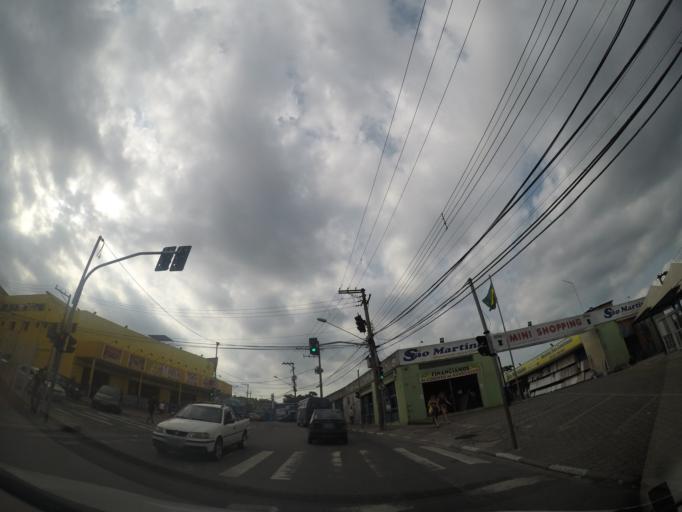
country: BR
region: Sao Paulo
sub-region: Guarulhos
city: Guarulhos
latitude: -23.4247
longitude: -46.5047
